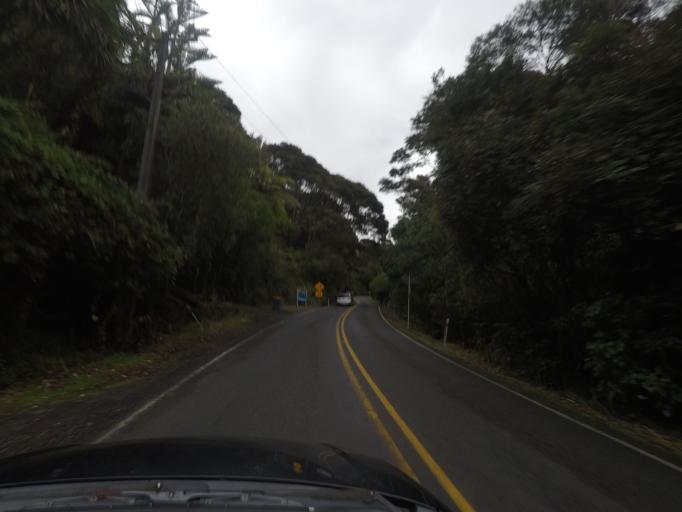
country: NZ
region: Auckland
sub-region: Auckland
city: Titirangi
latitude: -36.9322
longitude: 174.5870
